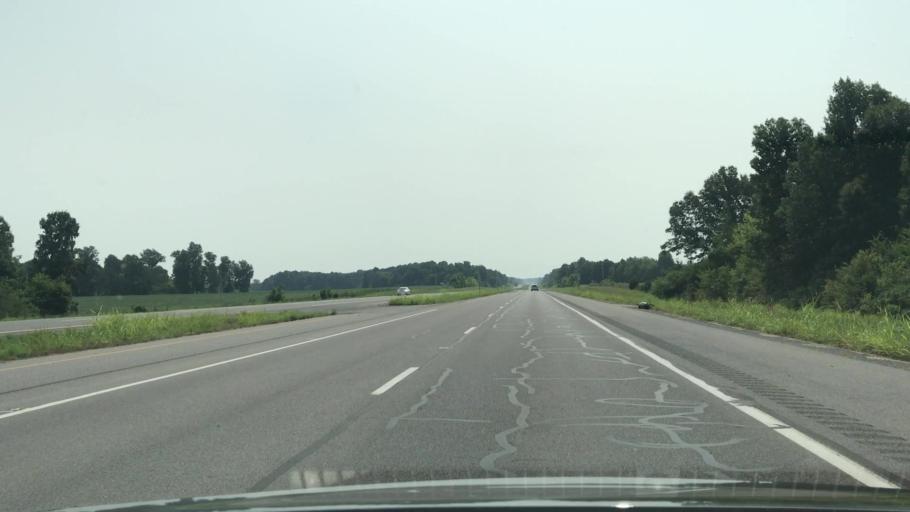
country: US
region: Kentucky
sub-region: Graves County
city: Mayfield
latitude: 36.6762
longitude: -88.5193
